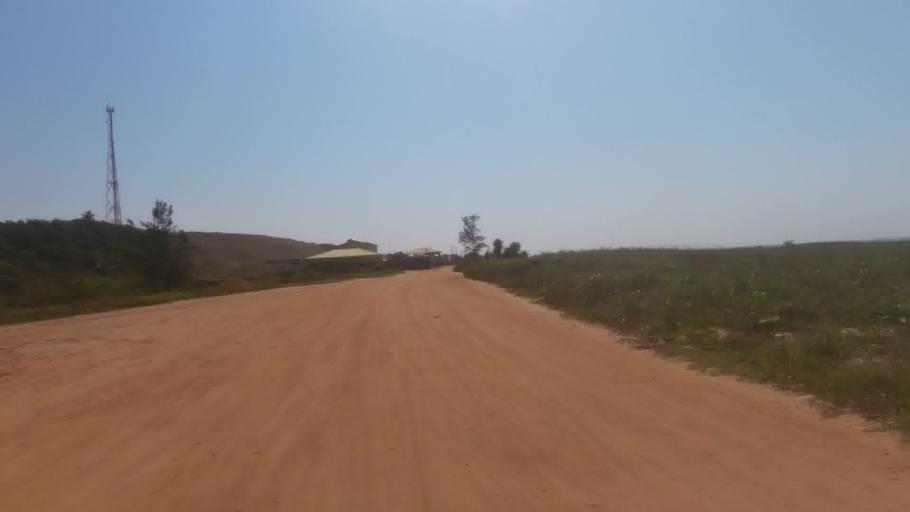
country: BR
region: Espirito Santo
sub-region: Marataizes
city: Marataizes
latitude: -21.1042
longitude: -40.8505
